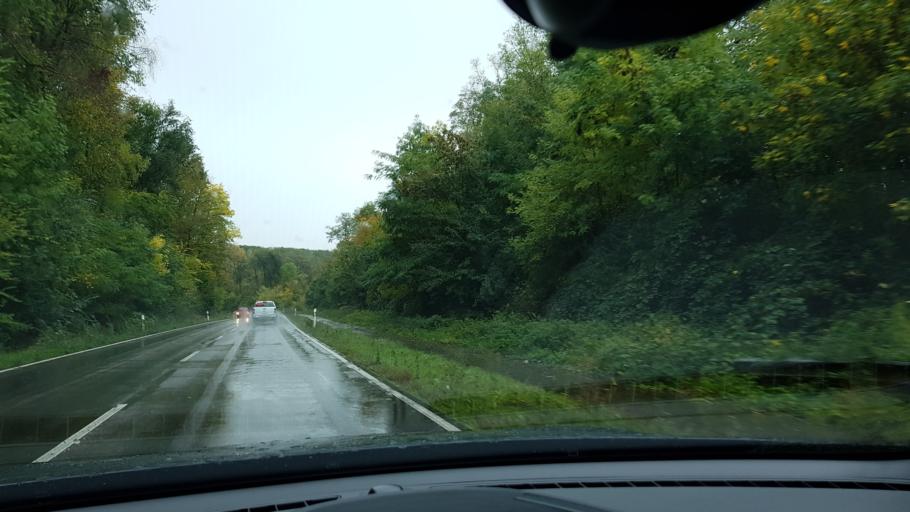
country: DE
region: North Rhine-Westphalia
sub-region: Regierungsbezirk Dusseldorf
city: Grevenbroich
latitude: 51.0408
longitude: 6.6008
